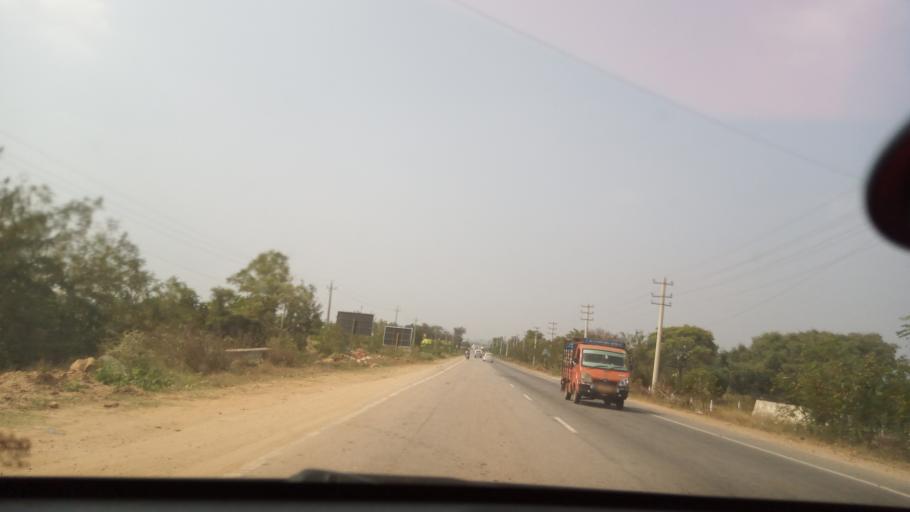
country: IN
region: Karnataka
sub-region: Chamrajnagar
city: Chamrajnagar
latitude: 11.9838
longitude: 76.8746
